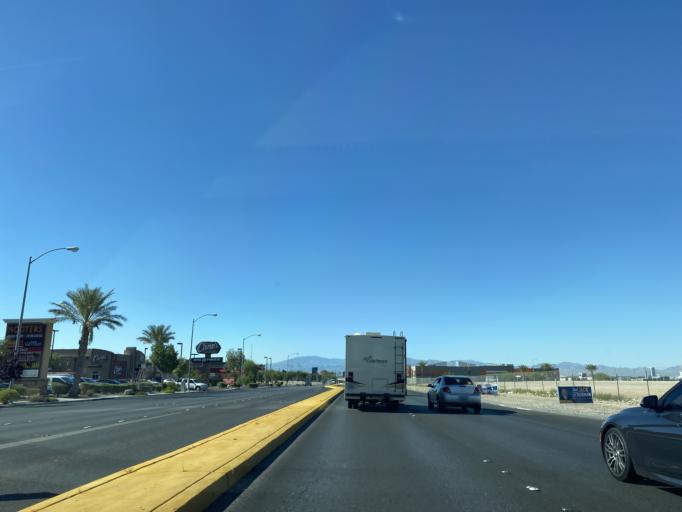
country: US
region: Nevada
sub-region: Clark County
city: Enterprise
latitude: 36.0577
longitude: -115.2428
